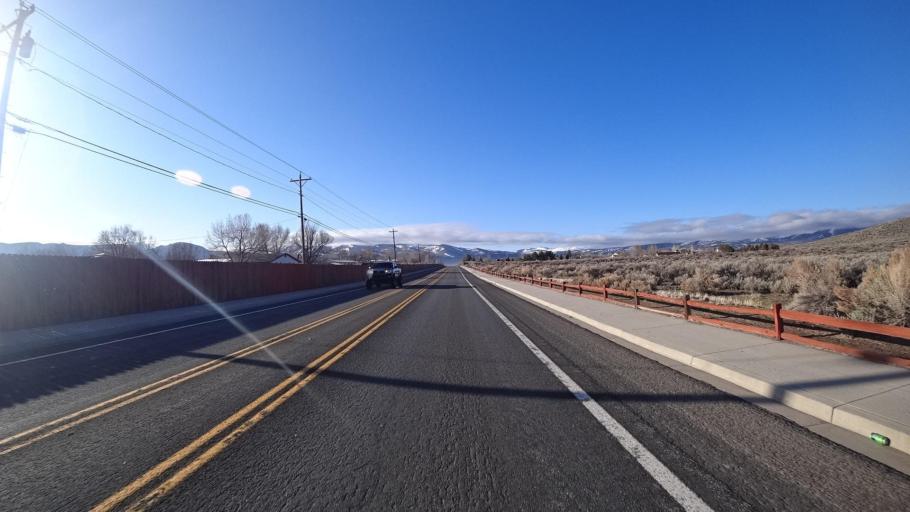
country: US
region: Nevada
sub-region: Washoe County
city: Cold Springs
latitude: 39.6855
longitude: -119.9785
